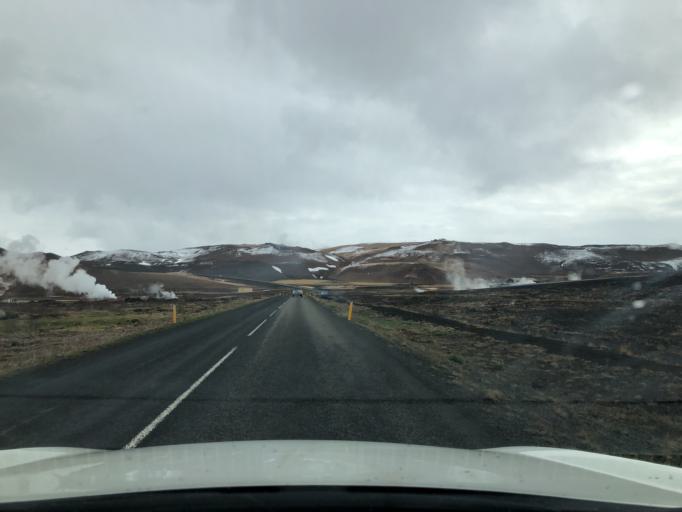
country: IS
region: Northeast
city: Laugar
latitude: 65.6392
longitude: -16.8572
